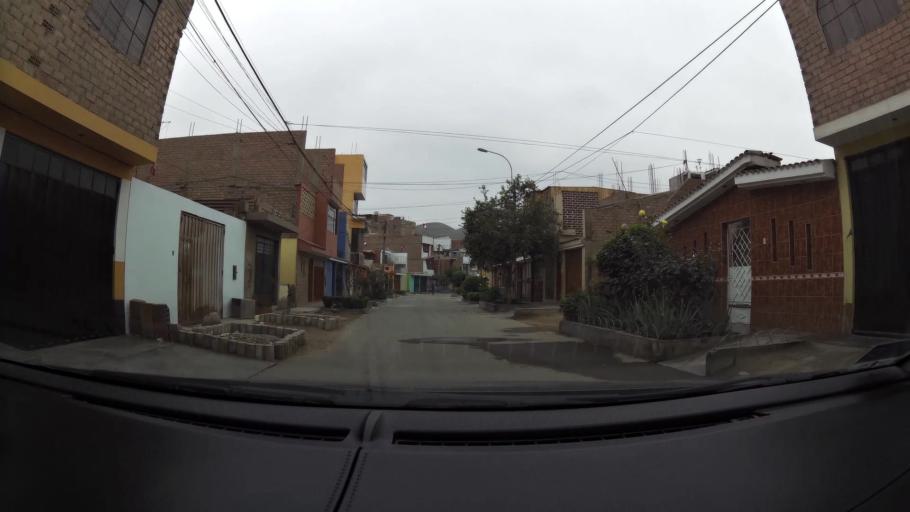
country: PE
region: Lima
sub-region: Lima
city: Independencia
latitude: -11.9450
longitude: -77.0869
